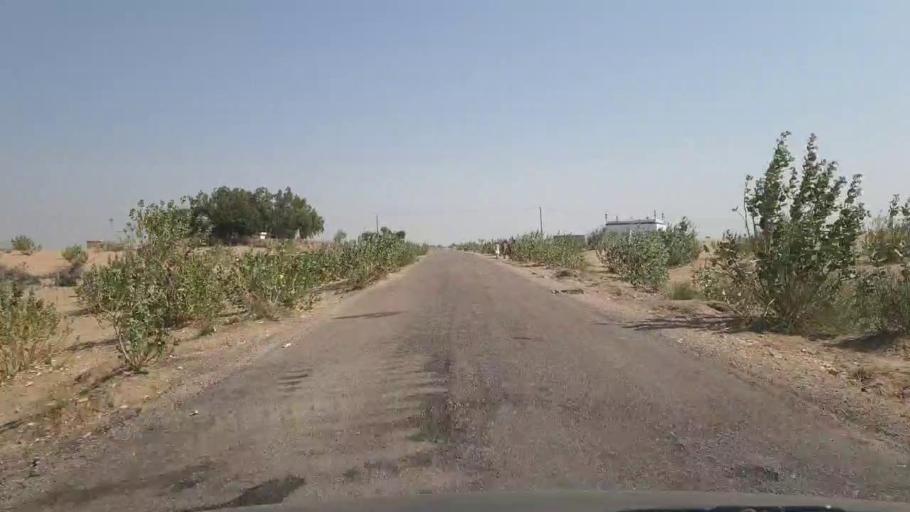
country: PK
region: Sindh
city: Chor
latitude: 25.6430
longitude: 70.0919
